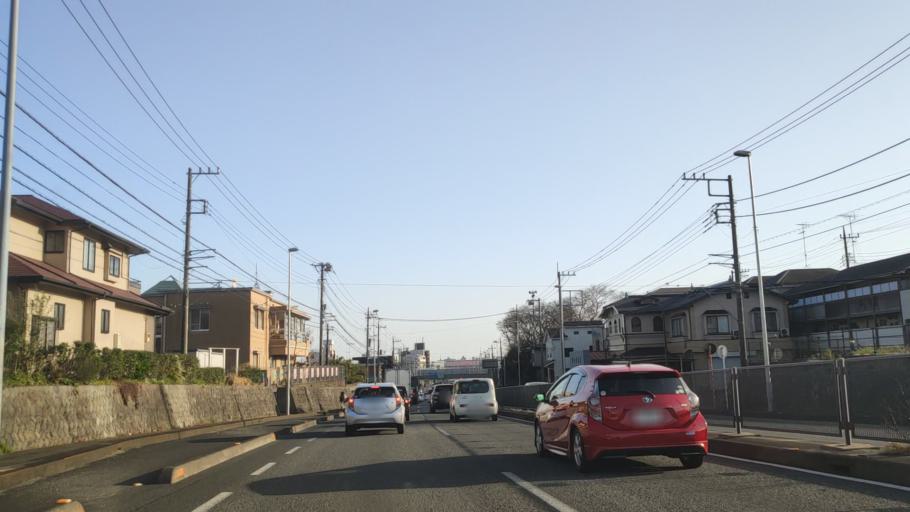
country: JP
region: Kanagawa
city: Zama
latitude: 35.4680
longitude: 139.3683
